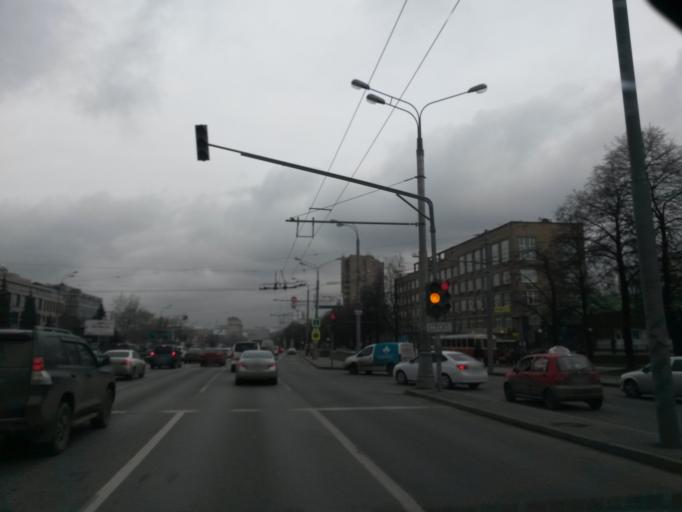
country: RU
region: Moscow
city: Kotlovka
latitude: 55.6833
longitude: 37.6237
